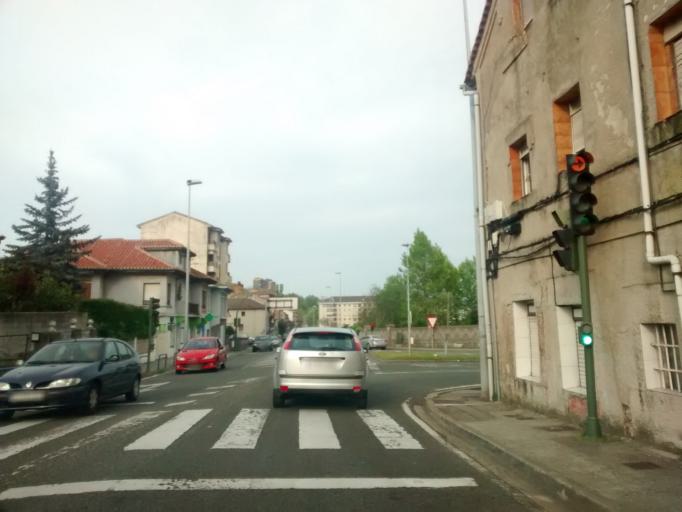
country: ES
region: Cantabria
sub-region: Provincia de Cantabria
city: Santander
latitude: 43.4538
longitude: -3.8467
